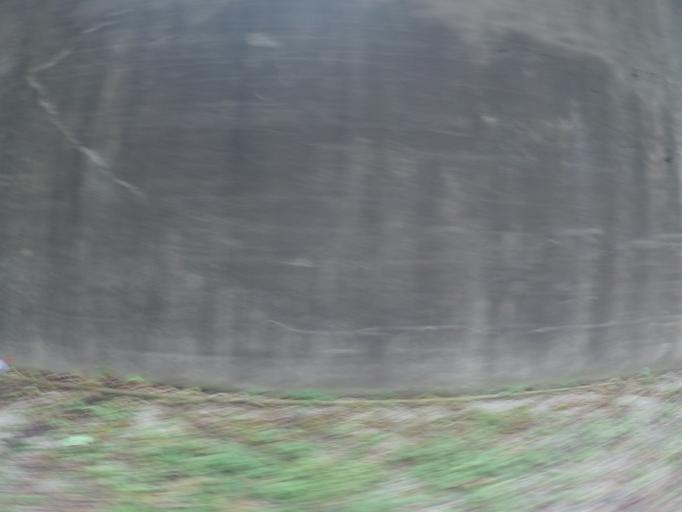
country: US
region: West Virginia
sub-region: Cabell County
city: Huntington
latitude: 38.4247
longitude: -82.3898
